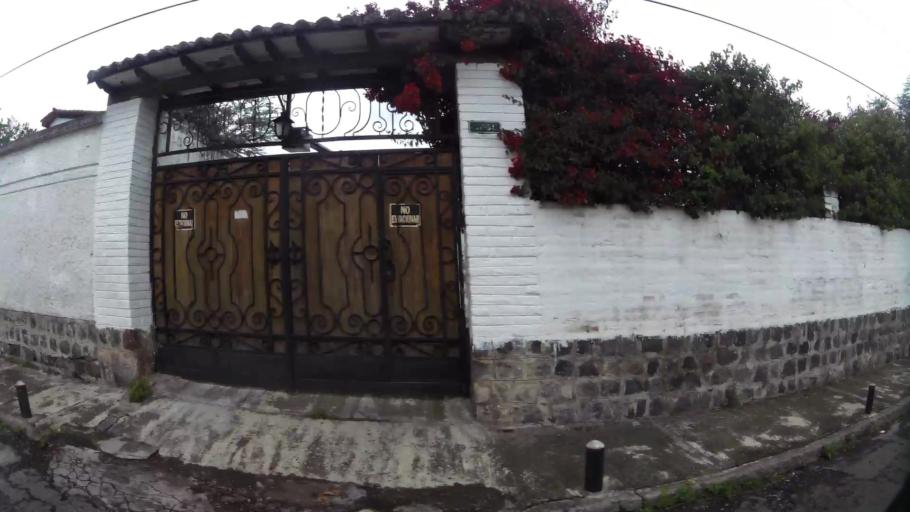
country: EC
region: Pichincha
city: Sangolqui
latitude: -0.3040
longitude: -78.4645
